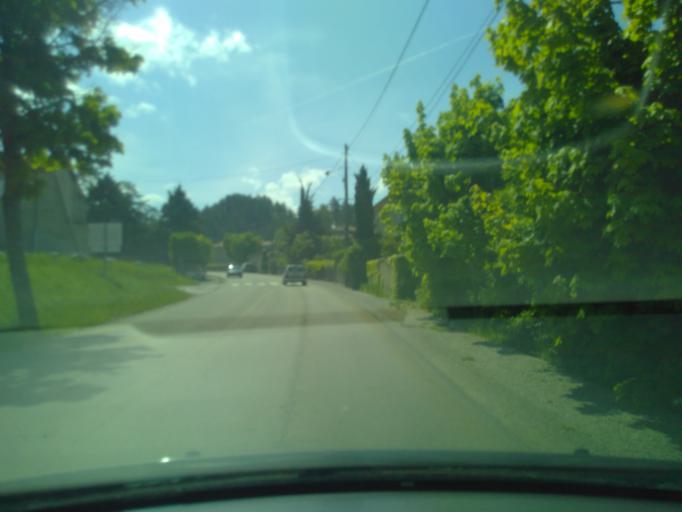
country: FR
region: Rhone-Alpes
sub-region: Departement de la Drome
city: Die
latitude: 44.6523
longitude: 5.4135
